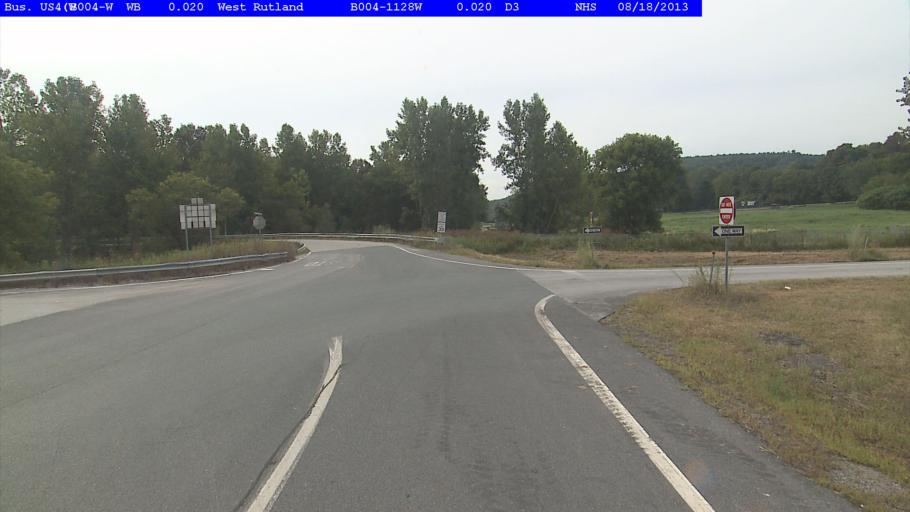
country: US
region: Vermont
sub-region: Rutland County
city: West Rutland
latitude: 43.5880
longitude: -73.0398
